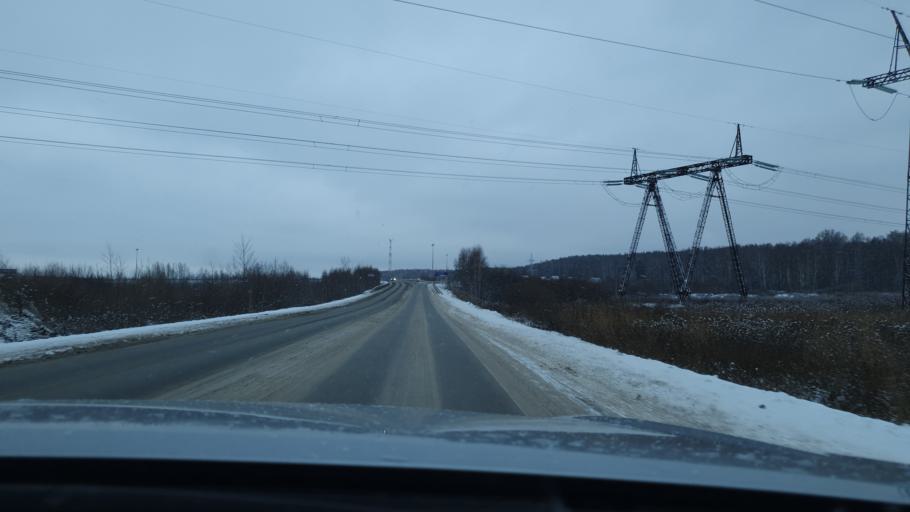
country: RU
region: Sverdlovsk
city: Istok
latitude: 56.7733
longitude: 60.7380
